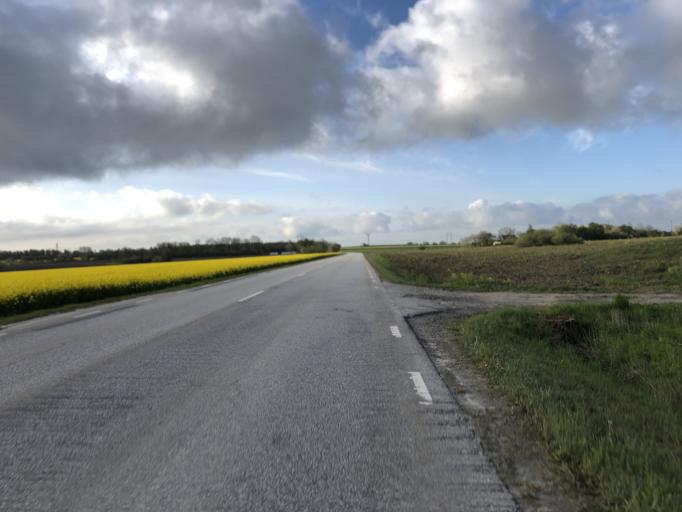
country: SE
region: Skane
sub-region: Lunds Kommun
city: Lund
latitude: 55.7036
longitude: 13.3035
